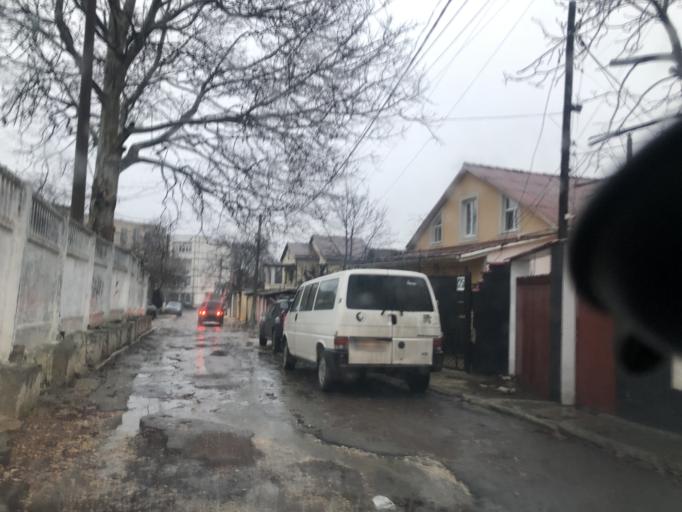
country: MD
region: Chisinau
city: Chisinau
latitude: 46.9847
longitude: 28.8508
